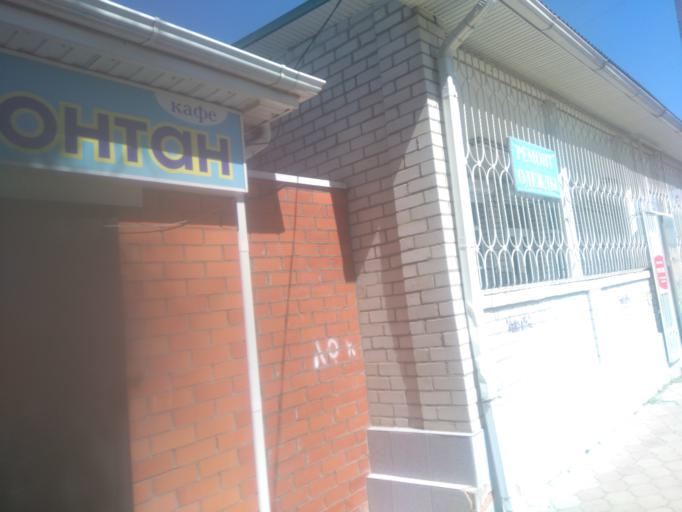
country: RU
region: Krasnodarskiy
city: Fastovetskaya
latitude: 45.9181
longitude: 40.1551
